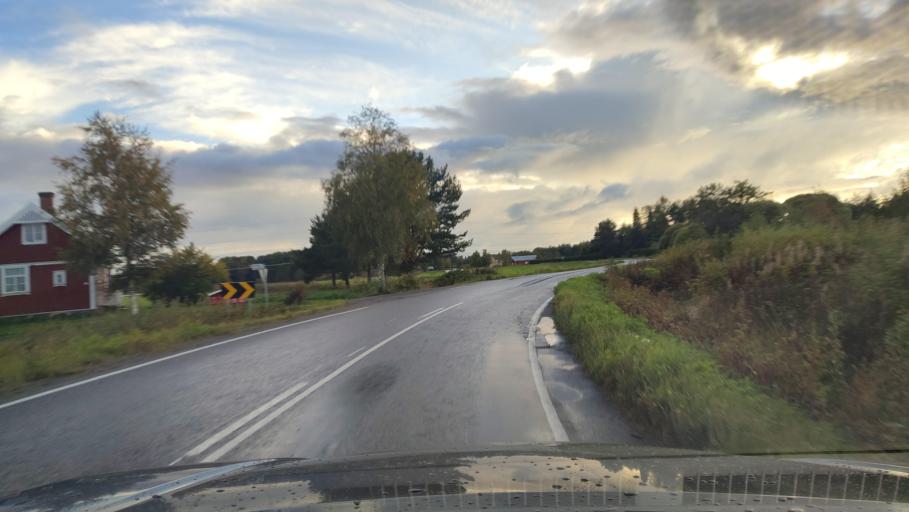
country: FI
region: Ostrobothnia
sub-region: Sydosterbotten
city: Kristinestad
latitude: 62.2896
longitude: 21.4278
